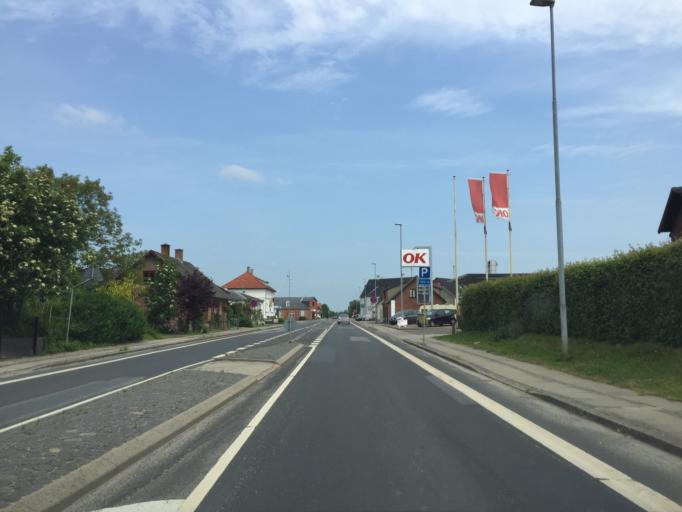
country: DK
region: South Denmark
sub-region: Svendborg Kommune
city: Thuro By
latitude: 55.1678
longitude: 10.7344
